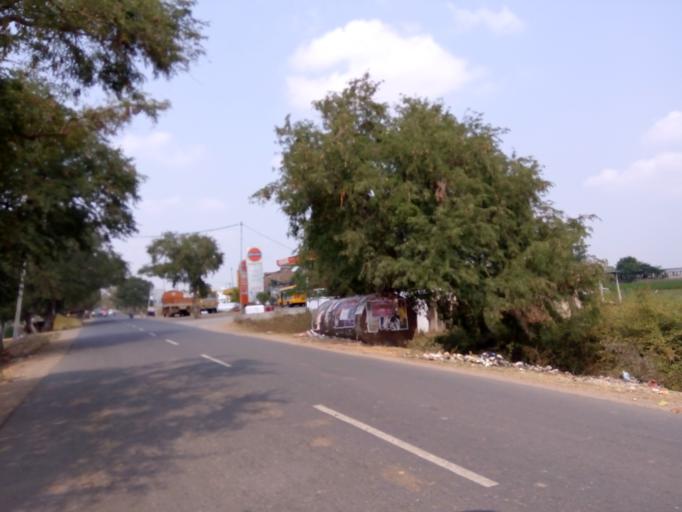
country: IN
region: Andhra Pradesh
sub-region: Prakasam
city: pedda nakkalapalem
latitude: 15.9601
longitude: 80.2801
